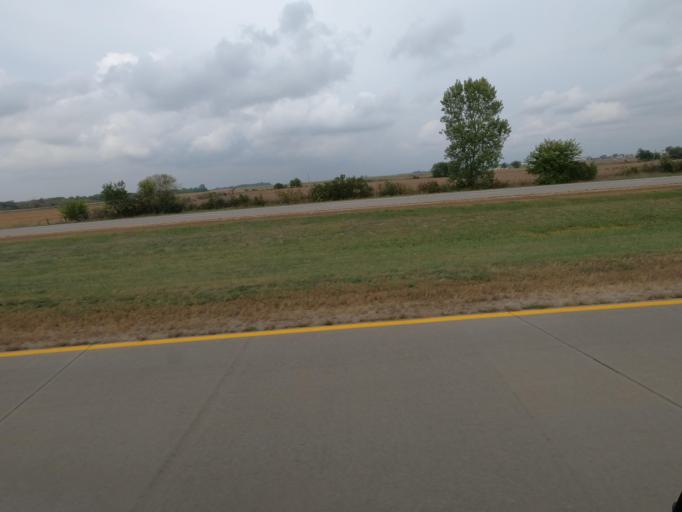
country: US
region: Iowa
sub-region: Wapello County
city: Ottumwa
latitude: 41.0954
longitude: -92.4526
